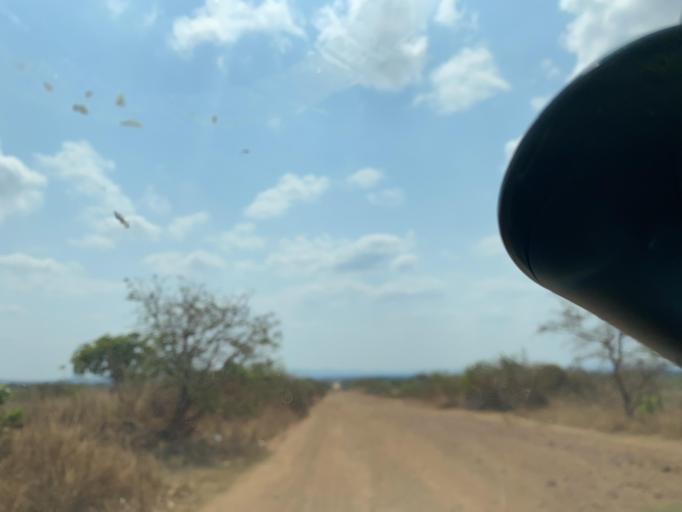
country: ZM
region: Lusaka
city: Chongwe
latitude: -15.5916
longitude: 28.7856
